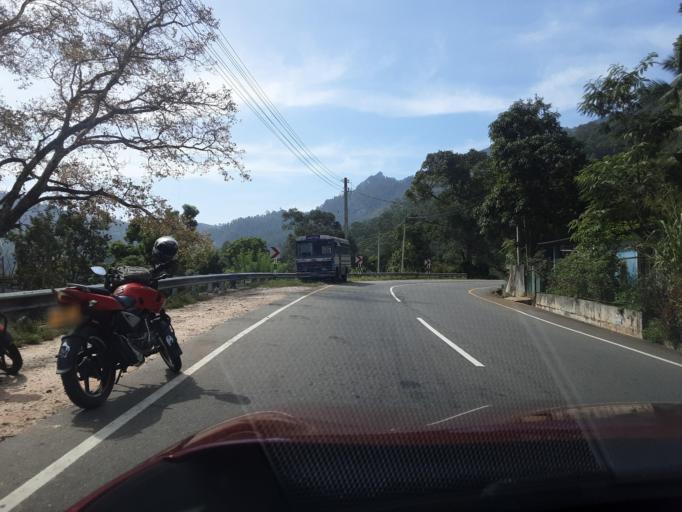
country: LK
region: Uva
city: Badulla
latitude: 6.9672
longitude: 81.0898
